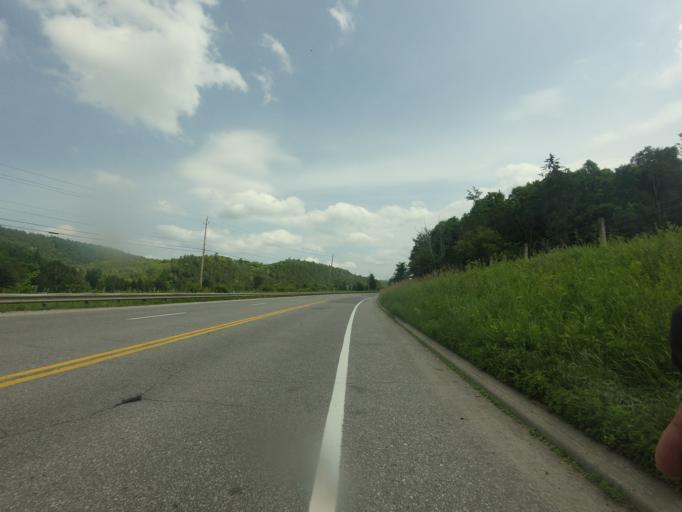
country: CA
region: Quebec
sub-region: Outaouais
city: Wakefield
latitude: 45.7590
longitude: -75.9203
